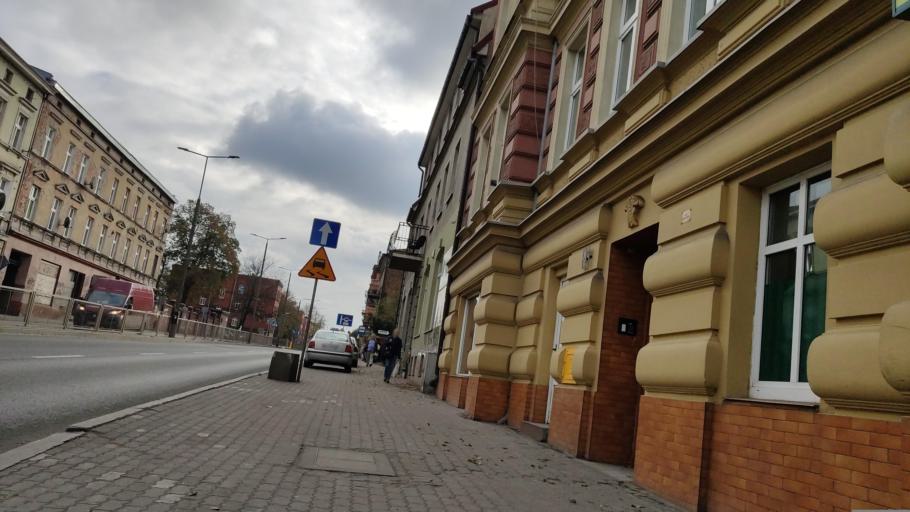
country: PL
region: Kujawsko-Pomorskie
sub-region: Powiat inowroclawski
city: Inowroclaw
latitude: 52.8052
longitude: 18.2478
